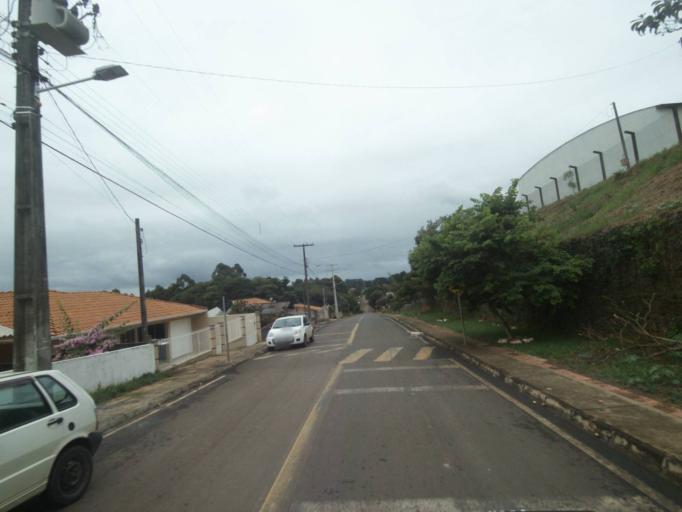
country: BR
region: Parana
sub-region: Telemaco Borba
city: Telemaco Borba
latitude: -24.3225
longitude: -50.6544
